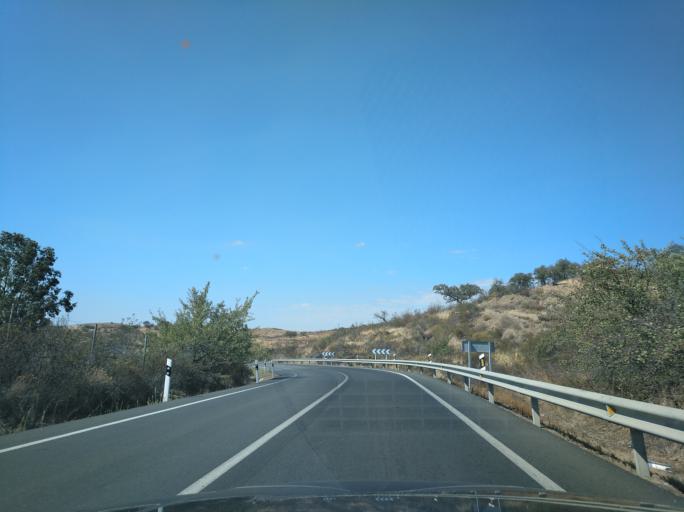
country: ES
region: Andalusia
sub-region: Provincia de Huelva
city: San Bartolome de la Torre
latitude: 37.4803
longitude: -7.1278
